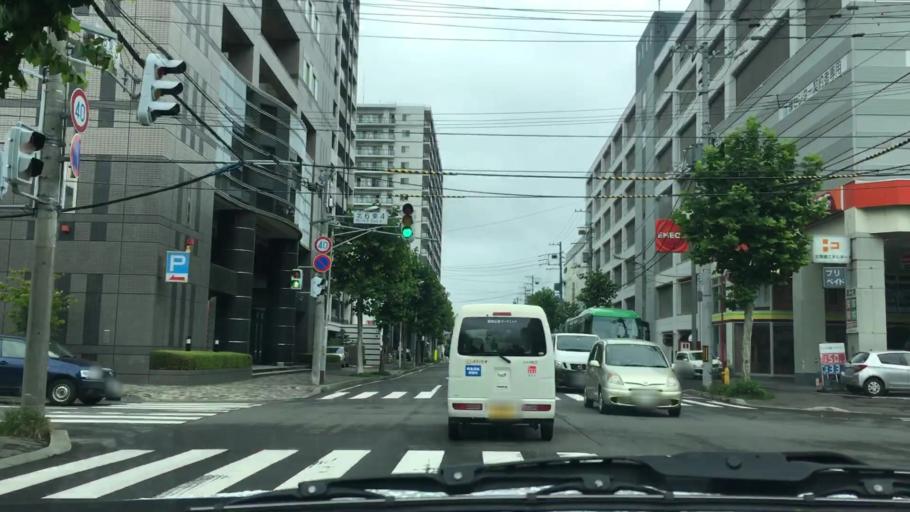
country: JP
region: Hokkaido
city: Sapporo
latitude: 43.0692
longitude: 141.3599
